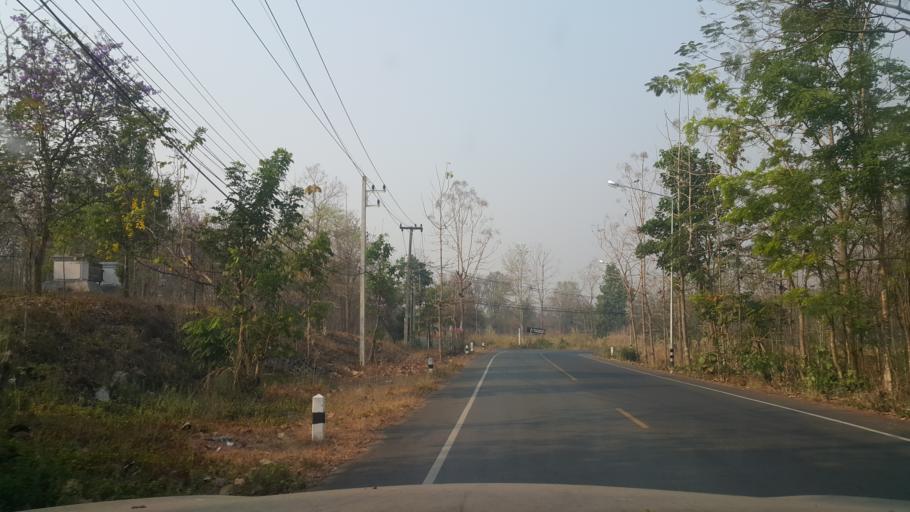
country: TH
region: Chiang Mai
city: Mae On
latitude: 18.7761
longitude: 99.2454
